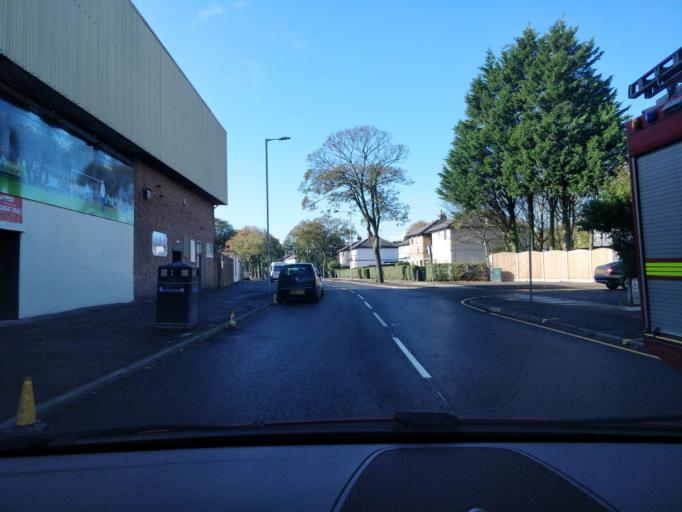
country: GB
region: England
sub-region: Sefton
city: Southport
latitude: 53.6386
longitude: -2.9792
